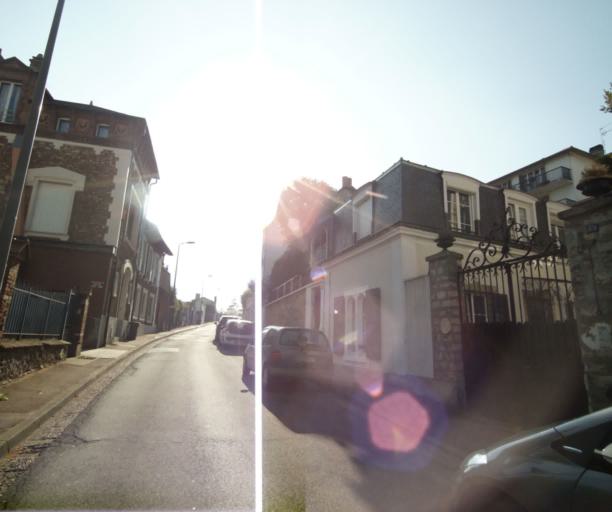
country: FR
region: Ile-de-France
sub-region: Departement des Hauts-de-Seine
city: Sevres
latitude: 48.8268
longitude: 2.2168
